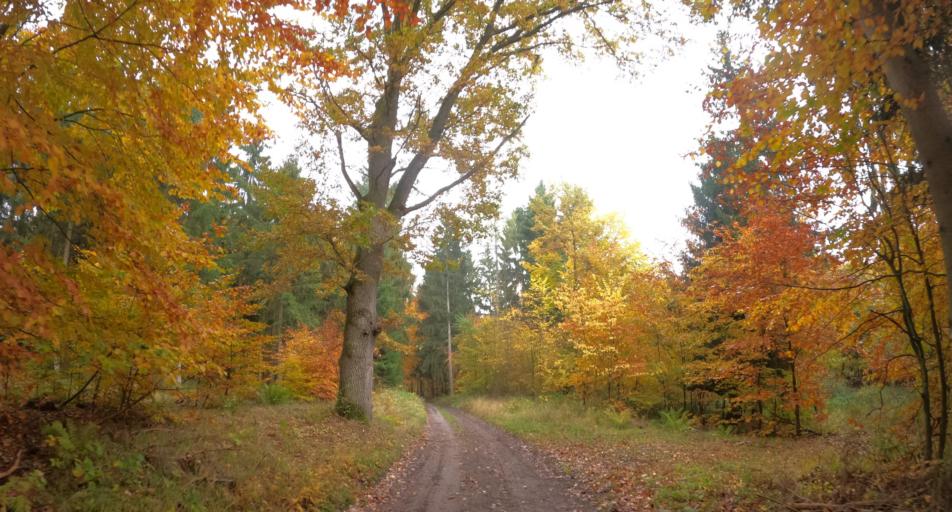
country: PL
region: West Pomeranian Voivodeship
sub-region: Powiat lobeski
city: Wegorzyno
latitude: 53.5252
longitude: 15.6617
